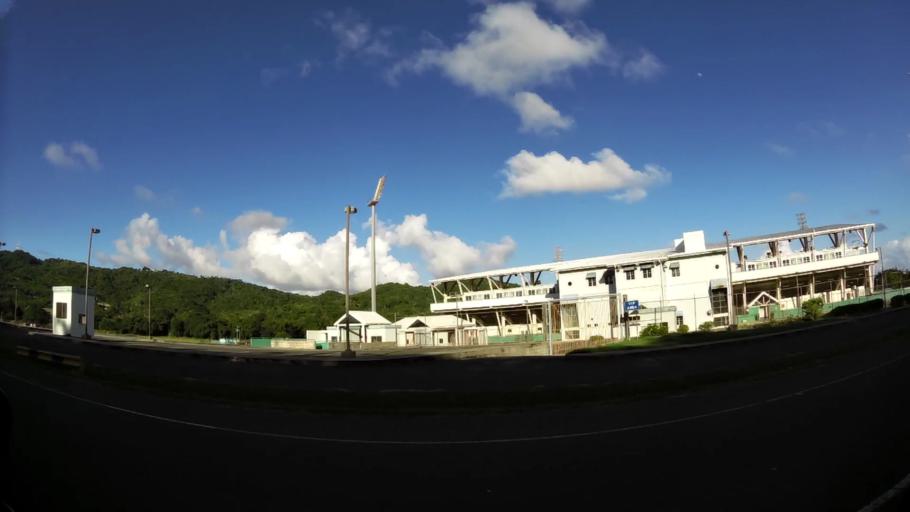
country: TT
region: Tobago
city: Scarborough
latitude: 11.1814
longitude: -60.7183
